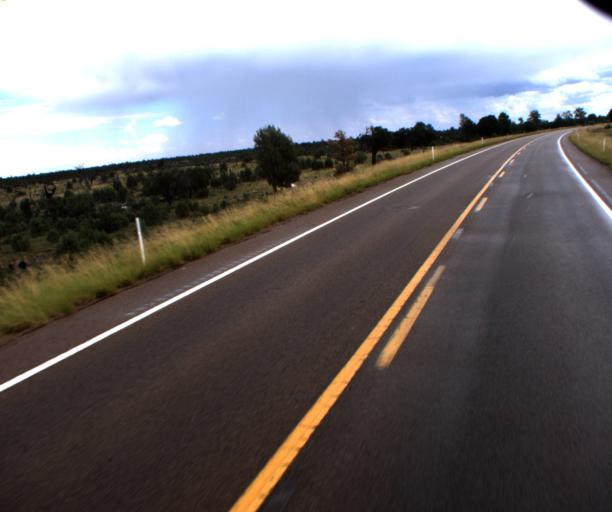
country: US
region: Arizona
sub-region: Navajo County
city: Heber-Overgaard
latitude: 34.3807
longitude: -110.4753
